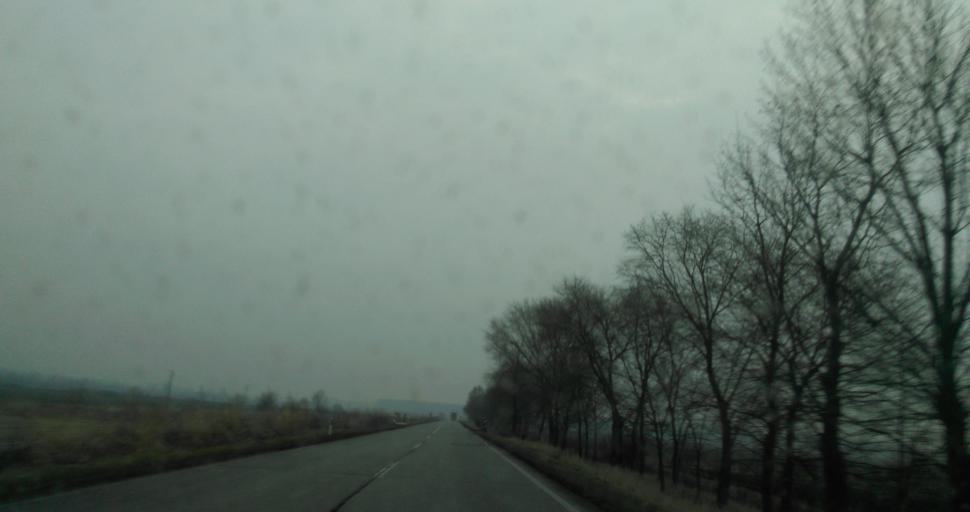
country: RS
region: Autonomna Pokrajina Vojvodina
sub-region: Srednjebanatski Okrug
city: Novi Becej
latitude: 45.5836
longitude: 20.0982
